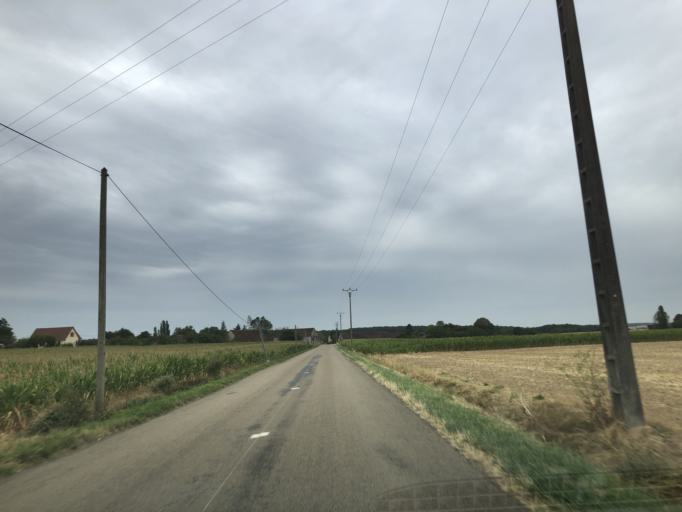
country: FR
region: Centre
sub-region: Departement du Loiret
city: Douchy
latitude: 47.9772
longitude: 3.1425
